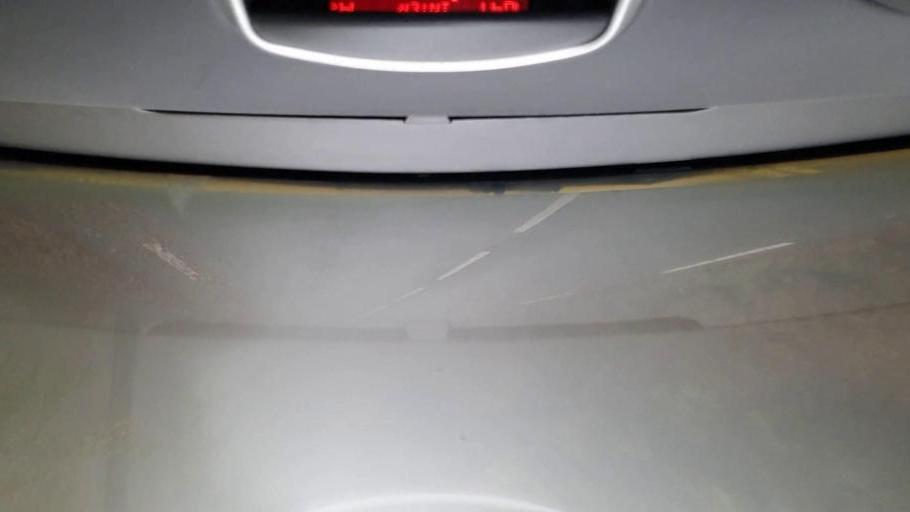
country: FR
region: Languedoc-Roussillon
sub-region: Departement du Gard
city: Valleraugue
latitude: 44.0925
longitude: 3.5582
